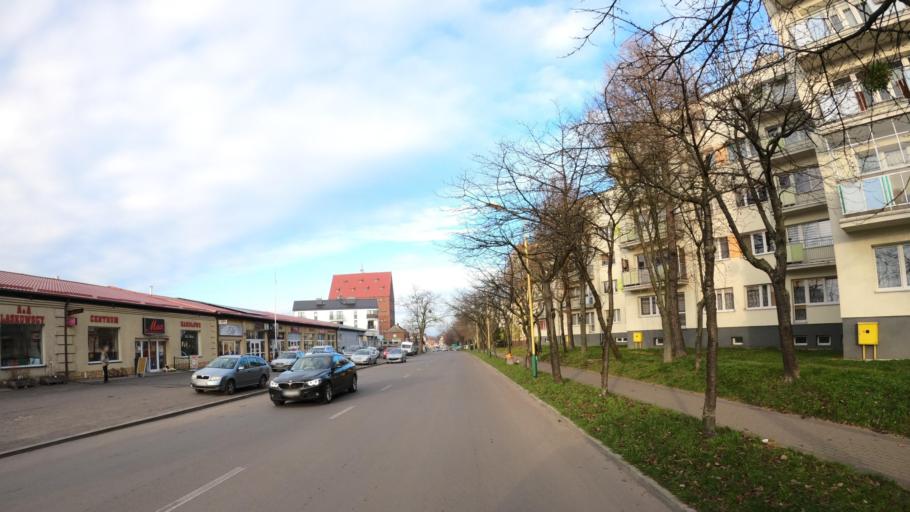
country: PL
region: West Pomeranian Voivodeship
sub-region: Powiat goleniowski
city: Nowogard
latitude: 53.6639
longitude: 15.1254
